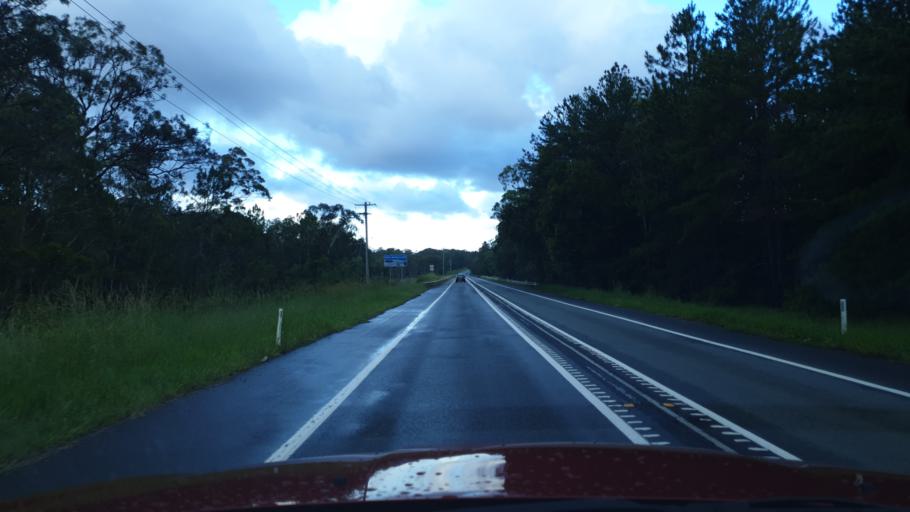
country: AU
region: Queensland
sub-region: Sunshine Coast
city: Little Mountain
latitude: -26.7995
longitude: 152.9859
